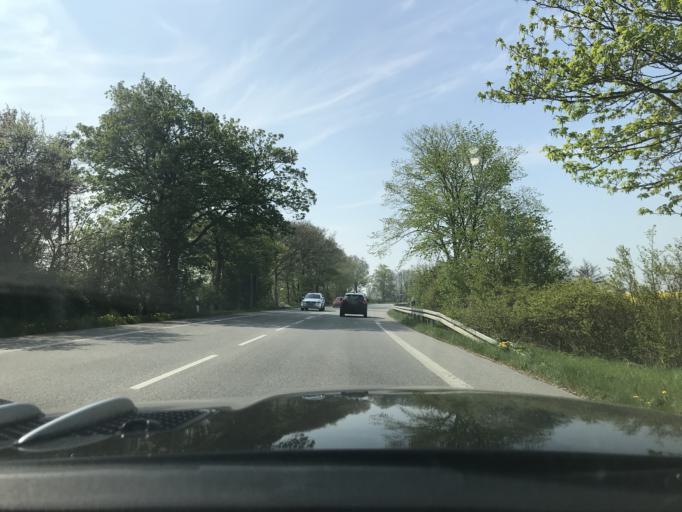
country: DE
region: Schleswig-Holstein
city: Gromitz
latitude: 54.1421
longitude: 10.9305
